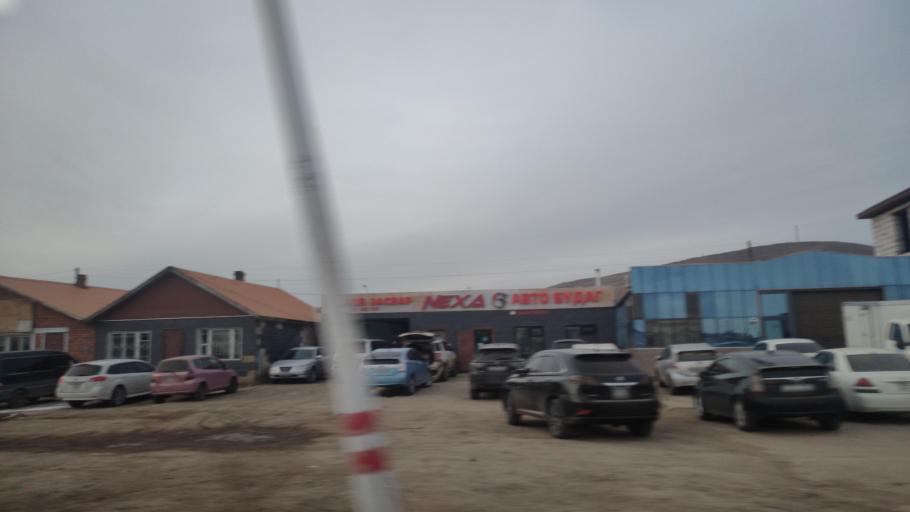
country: MN
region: Orhon
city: Erdenet
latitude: 49.0250
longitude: 104.0228
